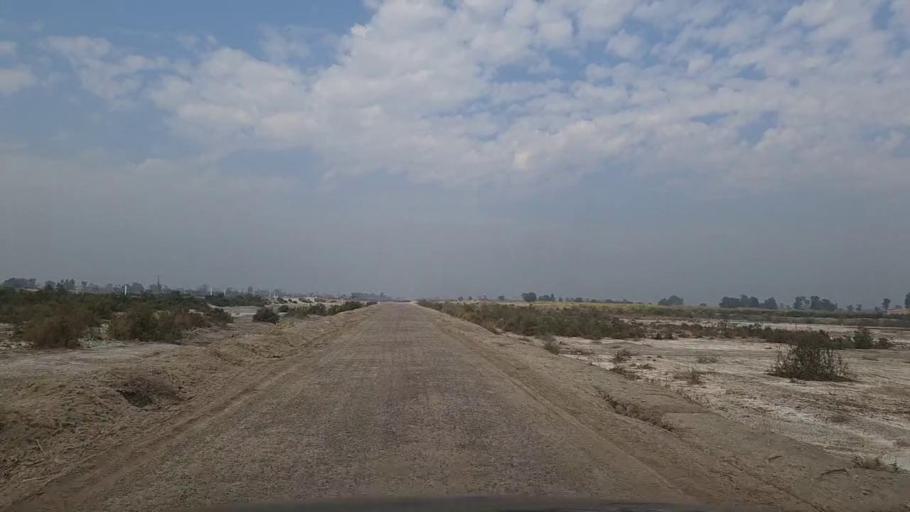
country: PK
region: Sindh
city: Daur
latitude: 26.3671
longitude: 68.3603
